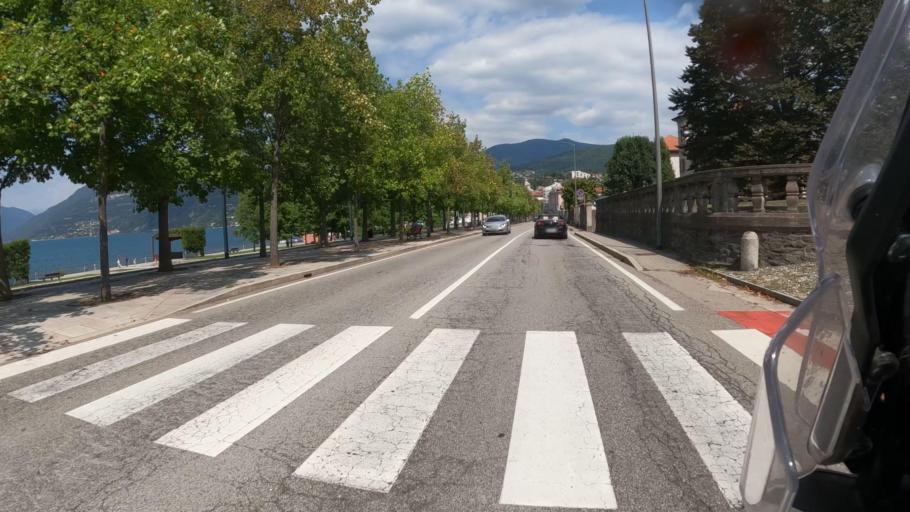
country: IT
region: Lombardy
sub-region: Provincia di Varese
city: Luino
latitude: 45.9999
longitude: 8.7369
